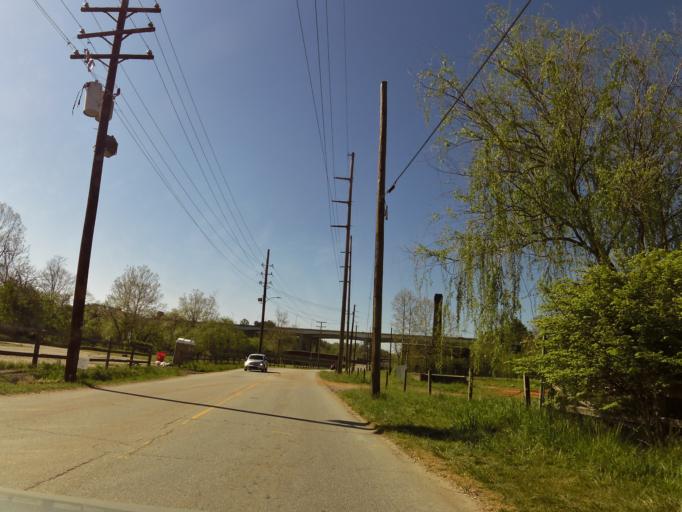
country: US
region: North Carolina
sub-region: Buncombe County
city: Asheville
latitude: 35.5881
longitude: -82.5694
